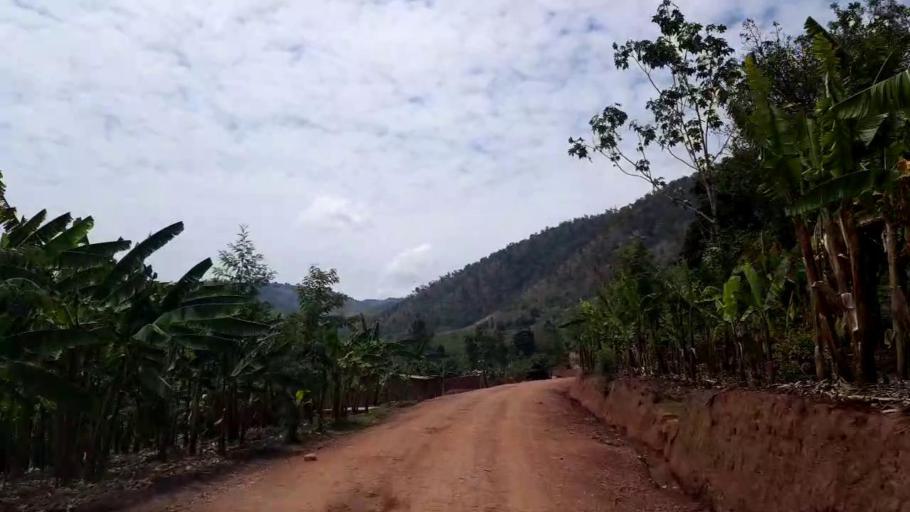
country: RW
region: Northern Province
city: Byumba
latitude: -1.4996
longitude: 30.1935
